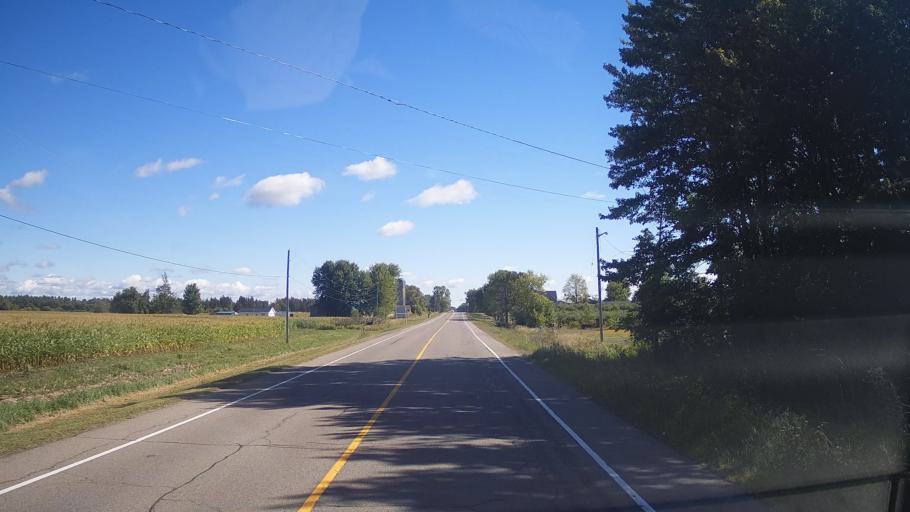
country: US
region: New York
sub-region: St. Lawrence County
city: Ogdensburg
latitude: 44.9420
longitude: -75.3031
